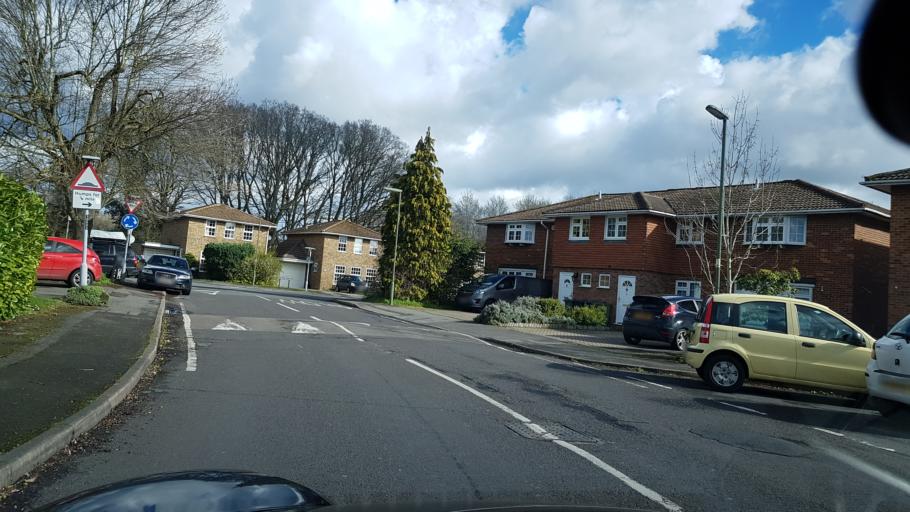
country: GB
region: England
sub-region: Surrey
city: Guildford
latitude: 51.2658
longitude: -0.5896
